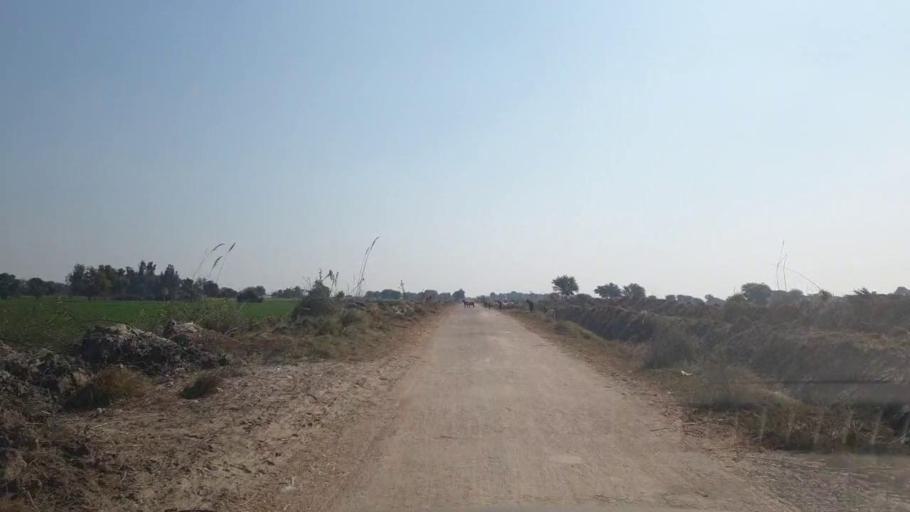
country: PK
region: Sindh
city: Shahdadpur
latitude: 25.9612
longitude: 68.6225
